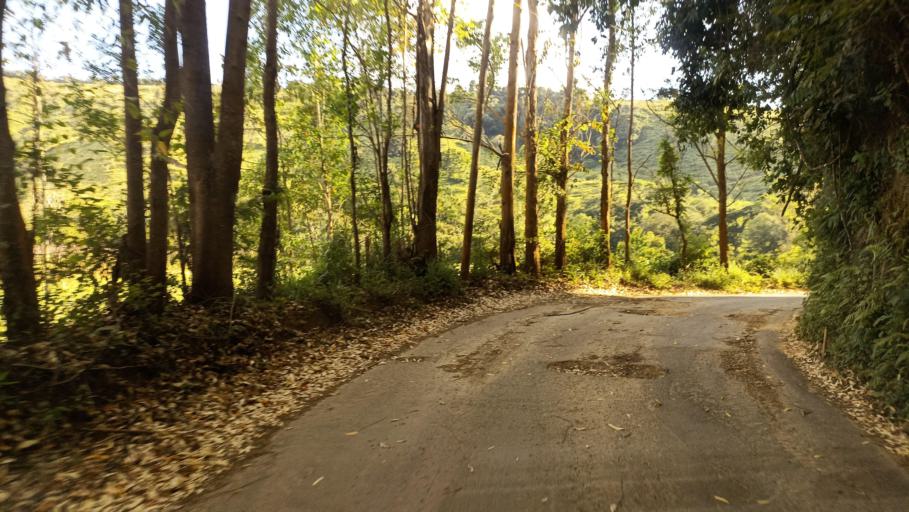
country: BR
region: Minas Gerais
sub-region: Ouro Preto
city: Ouro Preto
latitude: -20.3141
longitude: -43.5903
